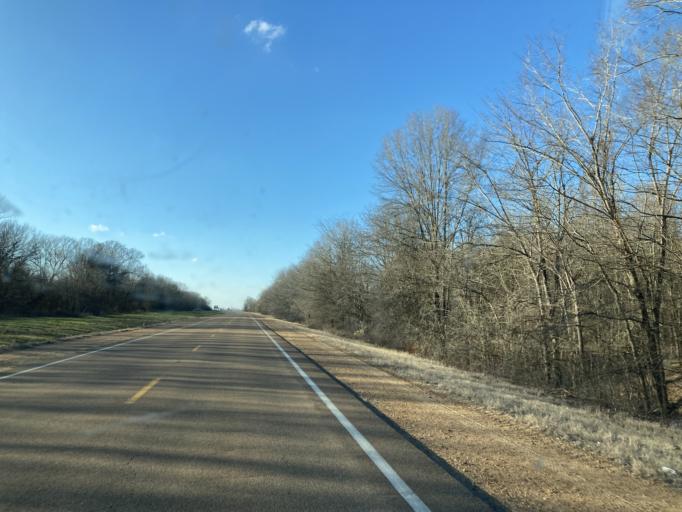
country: US
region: Mississippi
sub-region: Yazoo County
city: Yazoo City
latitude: 32.9214
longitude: -90.5634
